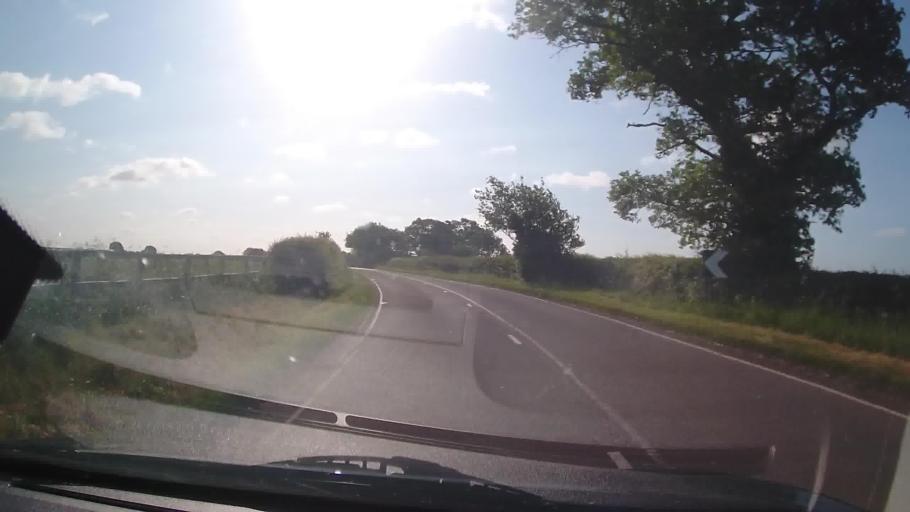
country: GB
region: England
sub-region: Shropshire
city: Shawbury
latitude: 52.7638
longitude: -2.6218
